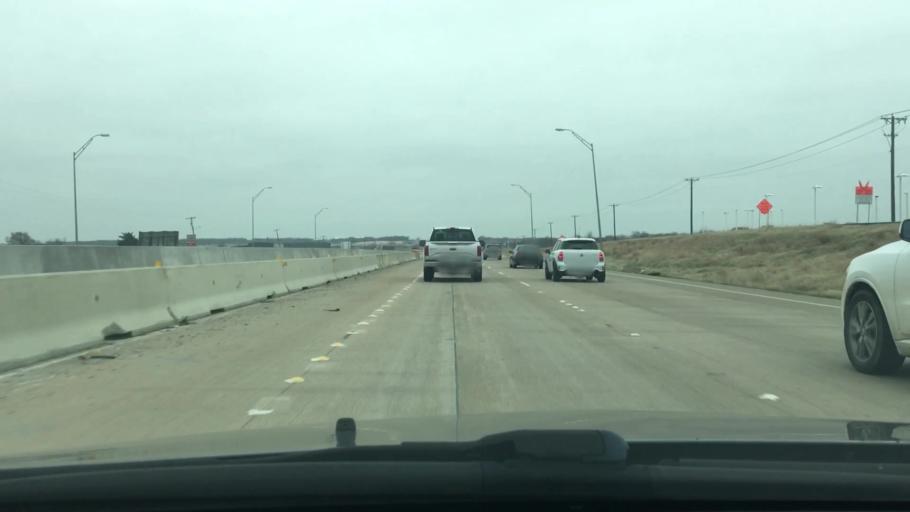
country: US
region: Texas
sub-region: Navarro County
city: Corsicana
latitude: 32.0573
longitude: -96.4513
